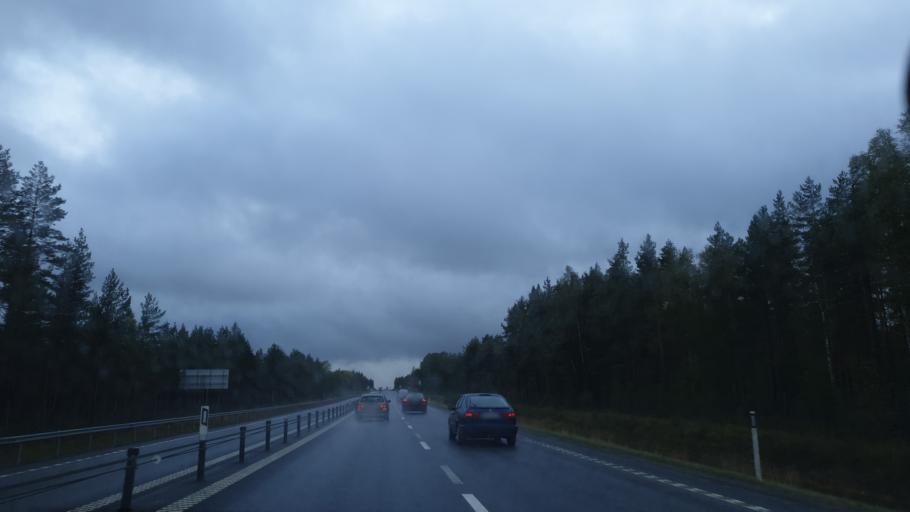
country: SE
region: Vaesterbotten
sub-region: Umea Kommun
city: Hoernefors
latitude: 63.6985
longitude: 20.0336
